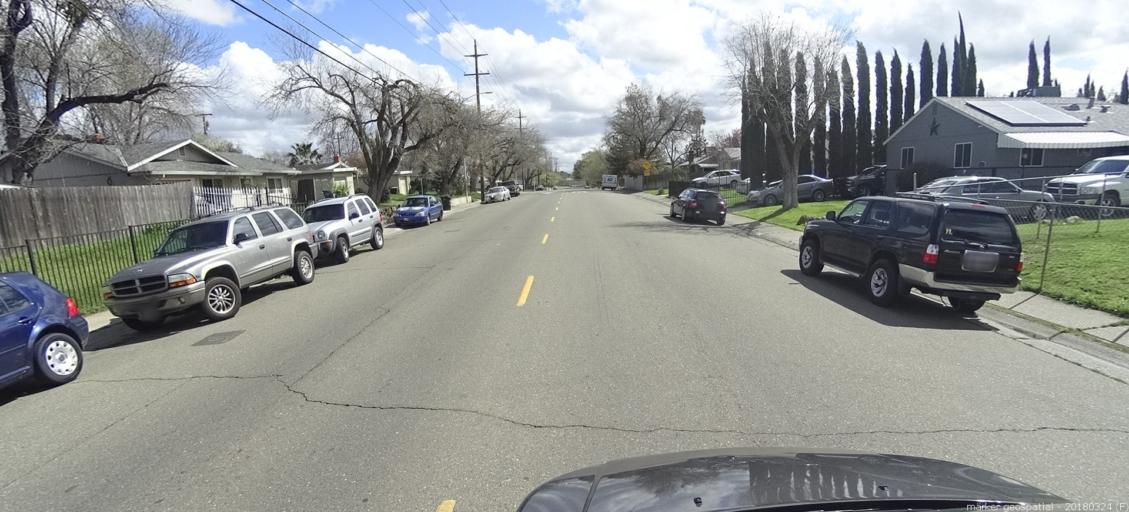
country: US
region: California
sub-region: Sacramento County
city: North Highlands
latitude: 38.6685
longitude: -121.3769
